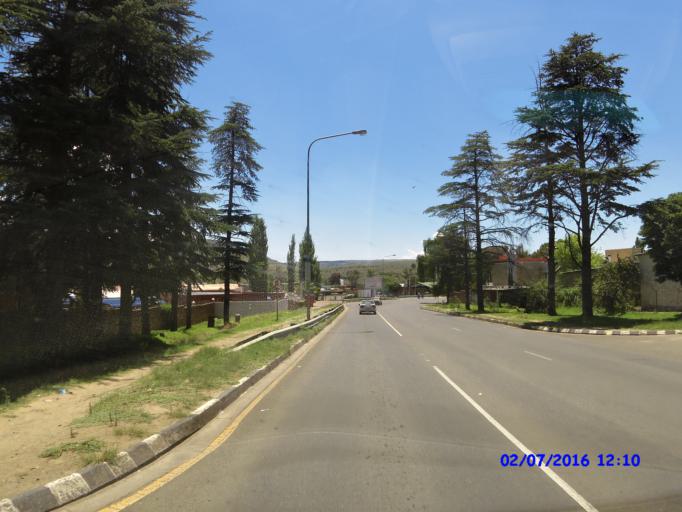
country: LS
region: Maseru
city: Maseru
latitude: -29.3002
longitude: 27.4689
